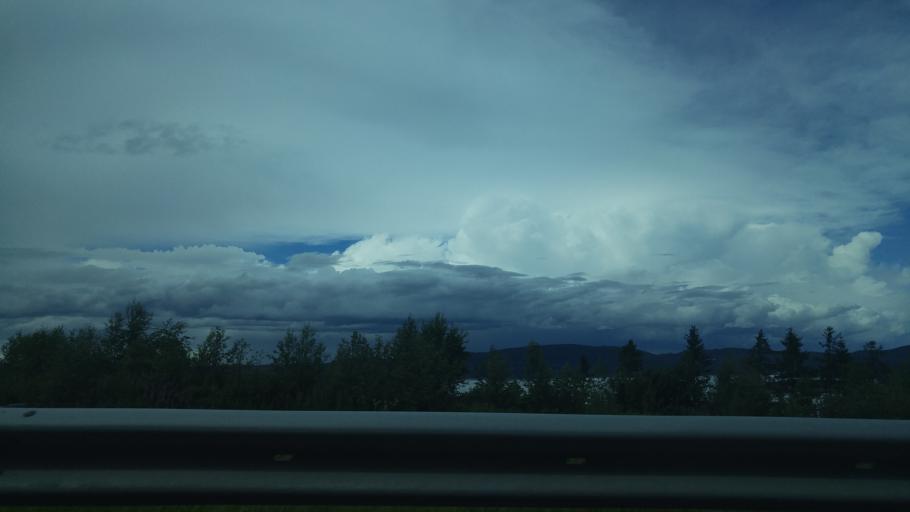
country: NO
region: Nord-Trondelag
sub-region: Stjordal
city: Stjordal
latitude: 63.5419
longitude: 10.8581
